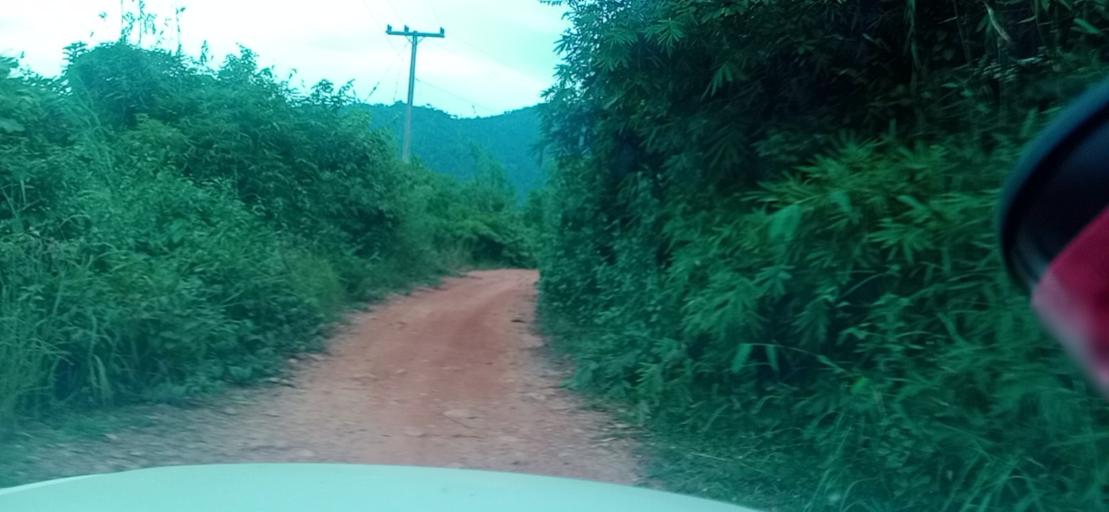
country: TH
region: Changwat Bueng Kan
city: Pak Khat
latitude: 18.5625
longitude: 103.2987
